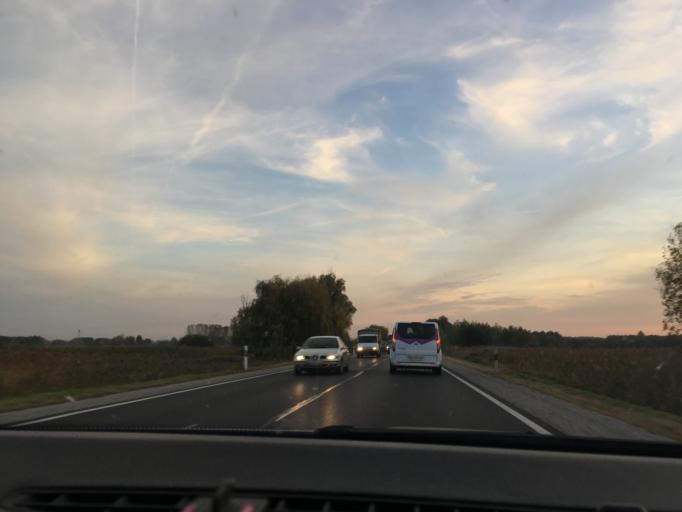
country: HU
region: Hajdu-Bihar
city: Hajduhadhaz
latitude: 47.7039
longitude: 21.6581
